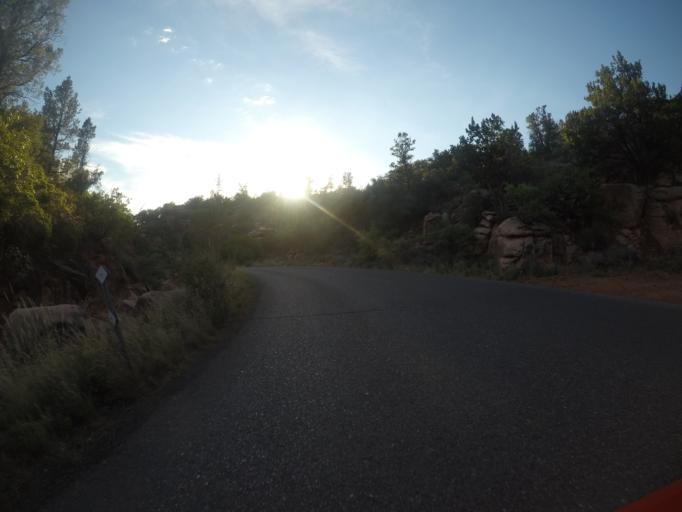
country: US
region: Arizona
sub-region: Yavapai County
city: West Sedona
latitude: 34.8267
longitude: -111.7846
